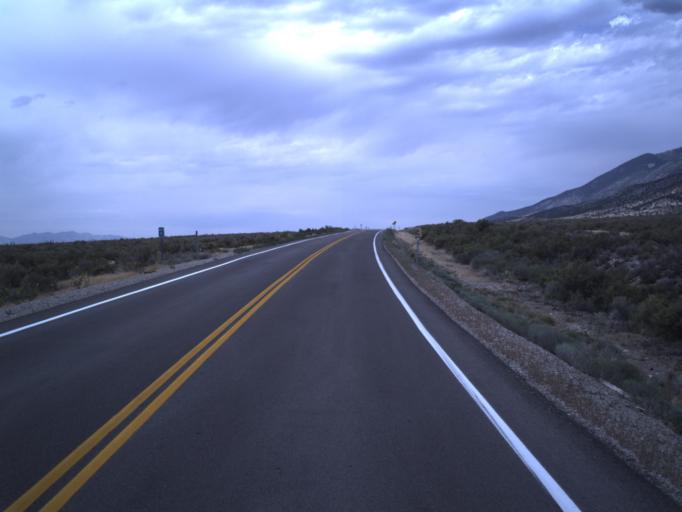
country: US
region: Utah
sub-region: Tooele County
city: Tooele
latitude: 40.2938
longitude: -112.2730
